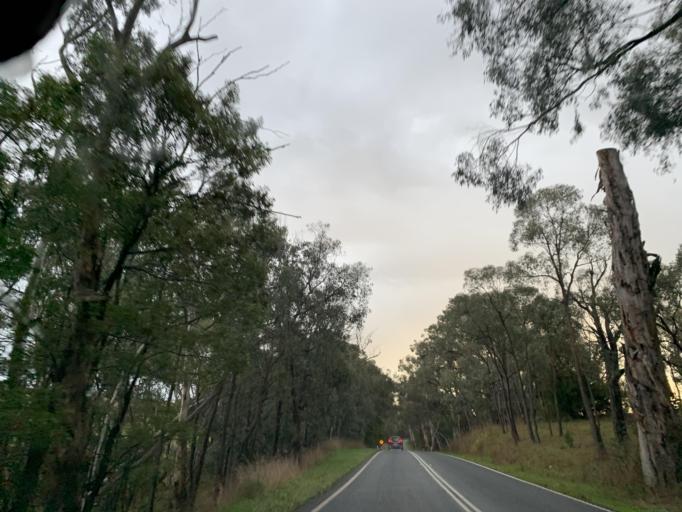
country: AU
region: Victoria
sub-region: Murrindindi
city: Kinglake West
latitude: -37.2211
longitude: 145.1197
